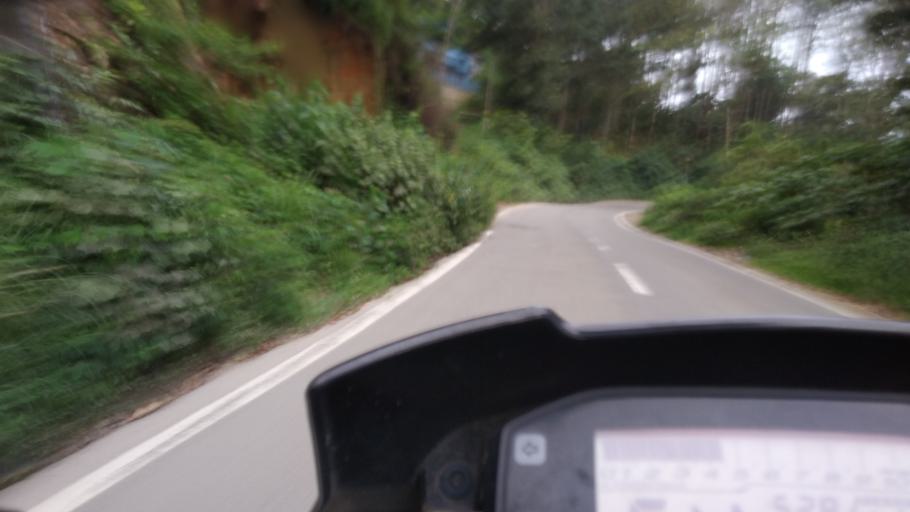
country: IN
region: Tamil Nadu
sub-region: Theni
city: Bodinayakkanur
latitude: 9.9976
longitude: 77.2199
